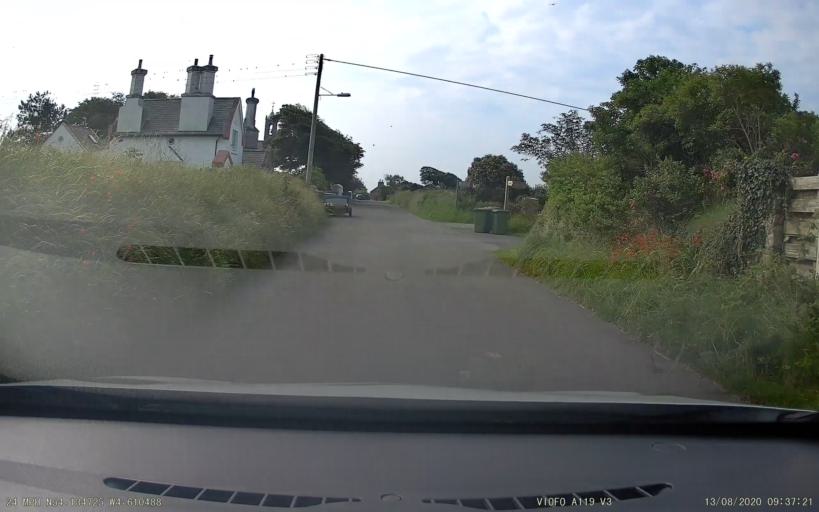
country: IM
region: Castletown
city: Castletown
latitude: 54.1347
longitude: -4.6105
